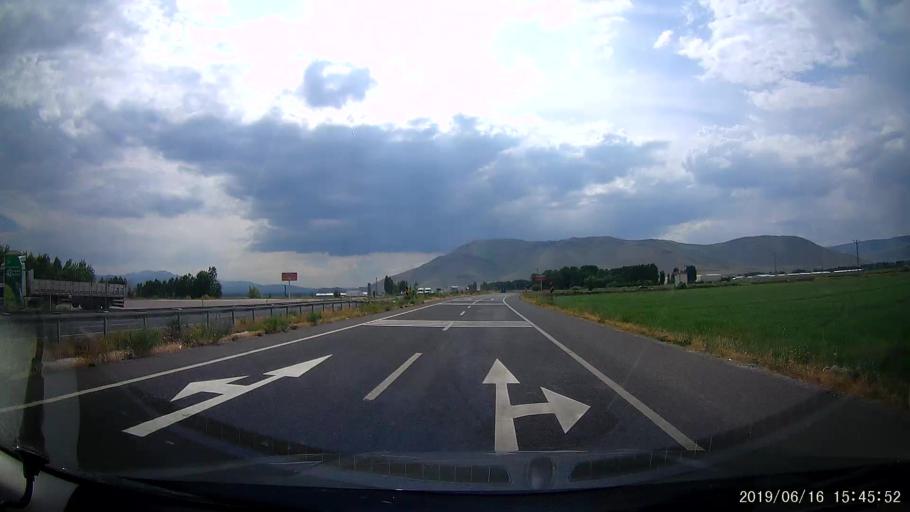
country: TR
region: Erzurum
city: Pasinler
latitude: 39.9894
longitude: 41.7566
